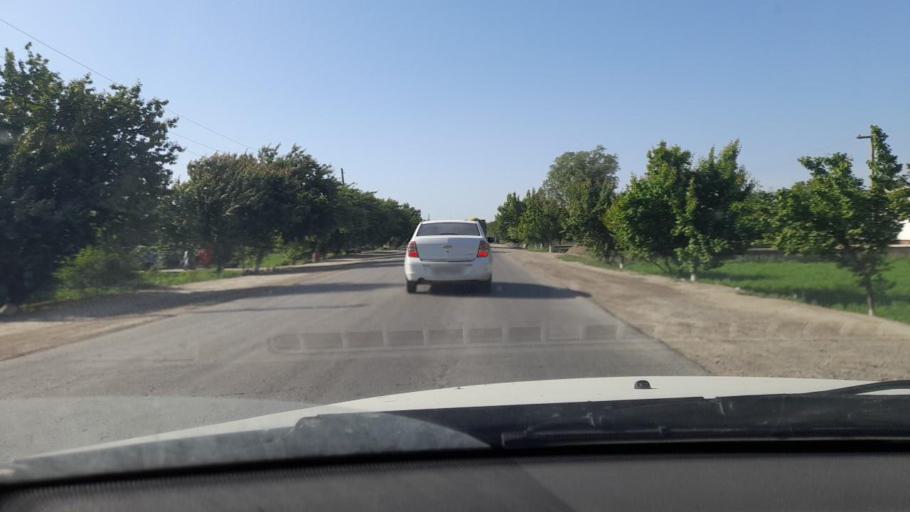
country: UZ
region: Bukhara
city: Romiton
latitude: 40.0586
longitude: 64.3277
